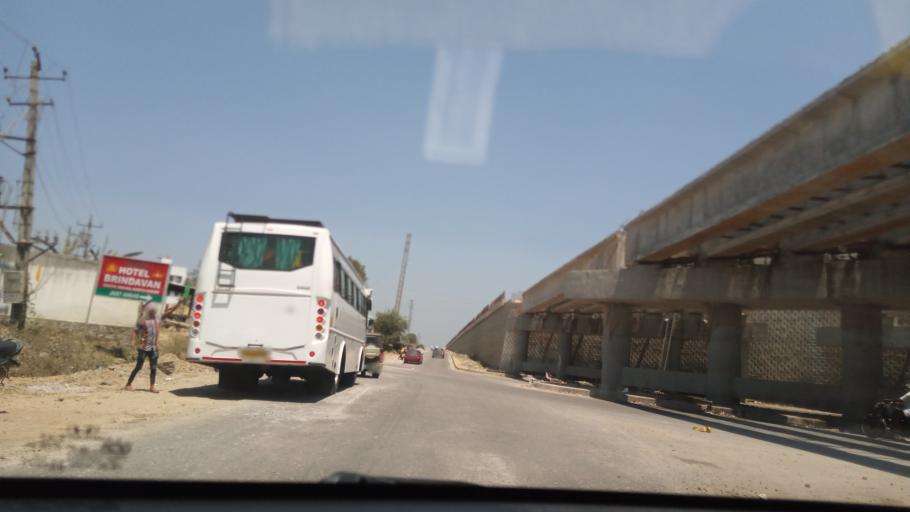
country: IN
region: Andhra Pradesh
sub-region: Chittoor
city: Pakala
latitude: 13.3551
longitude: 79.0853
